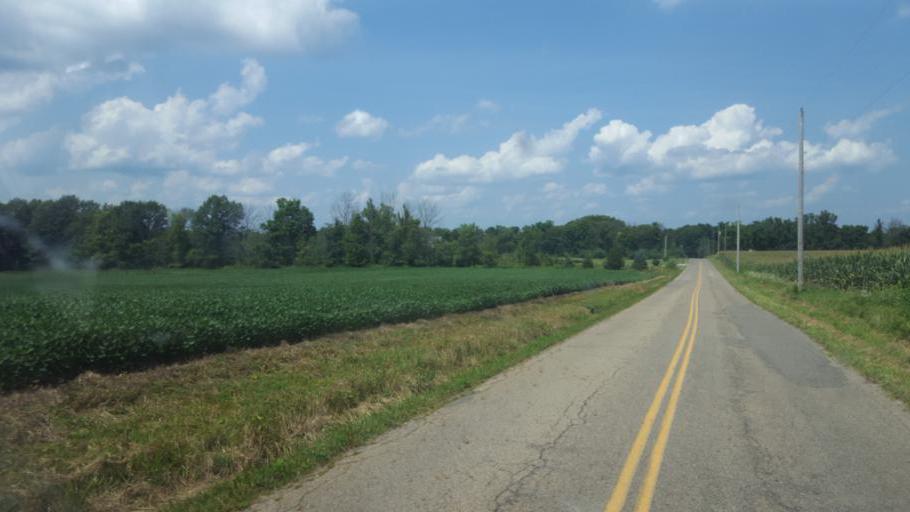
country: US
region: Ohio
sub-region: Knox County
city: Fredericktown
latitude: 40.4090
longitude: -82.5970
